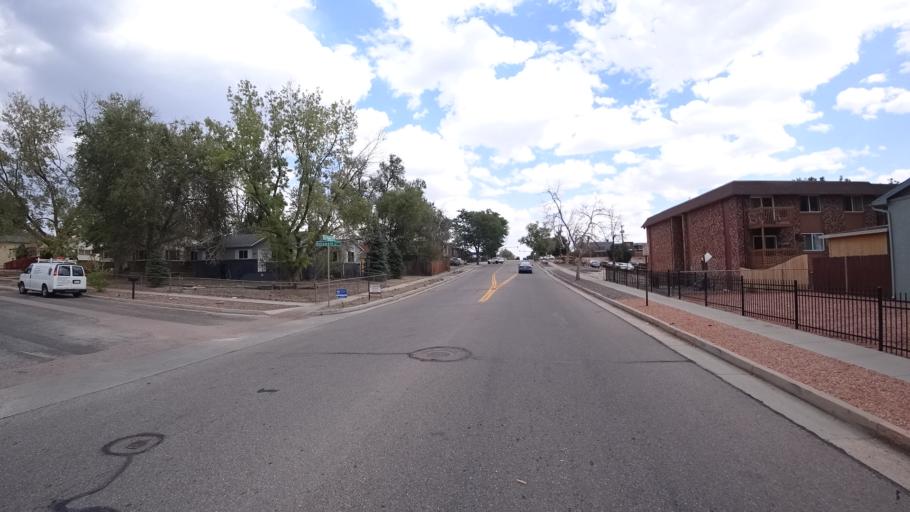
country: US
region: Colorado
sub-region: El Paso County
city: Cimarron Hills
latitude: 38.8512
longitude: -104.7595
